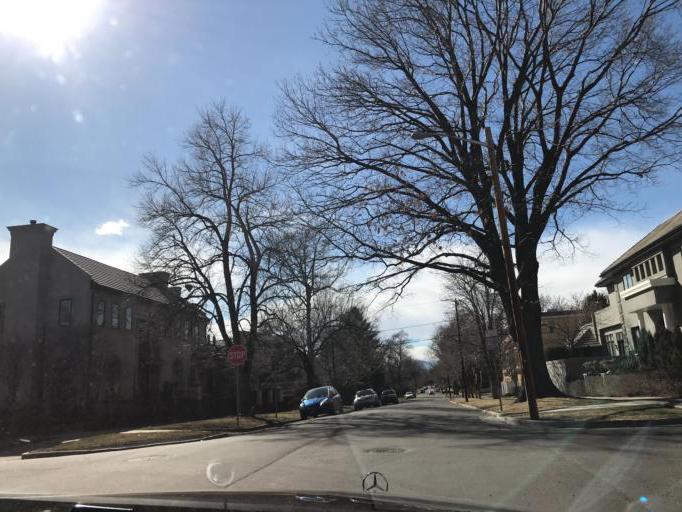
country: US
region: Colorado
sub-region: Arapahoe County
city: Glendale
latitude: 39.7225
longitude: -104.9508
